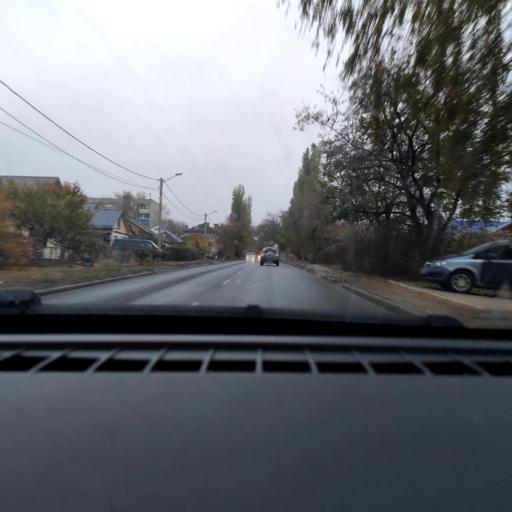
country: RU
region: Voronezj
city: Maslovka
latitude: 51.6213
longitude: 39.2520
